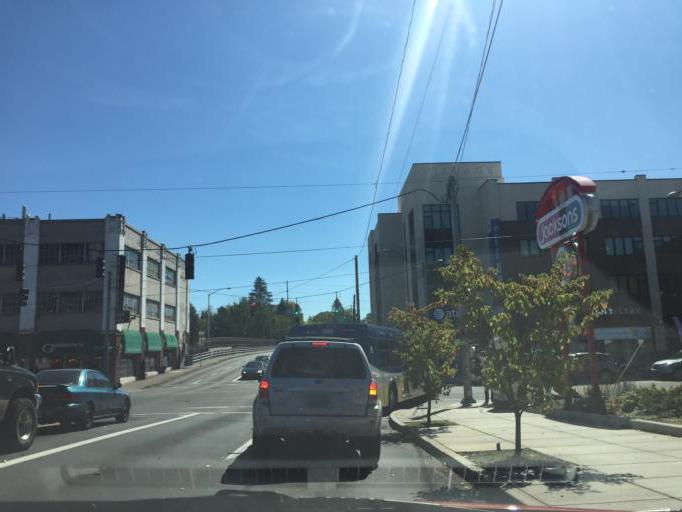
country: US
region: Oregon
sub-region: Multnomah County
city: Portland
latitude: 45.5355
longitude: -122.6308
